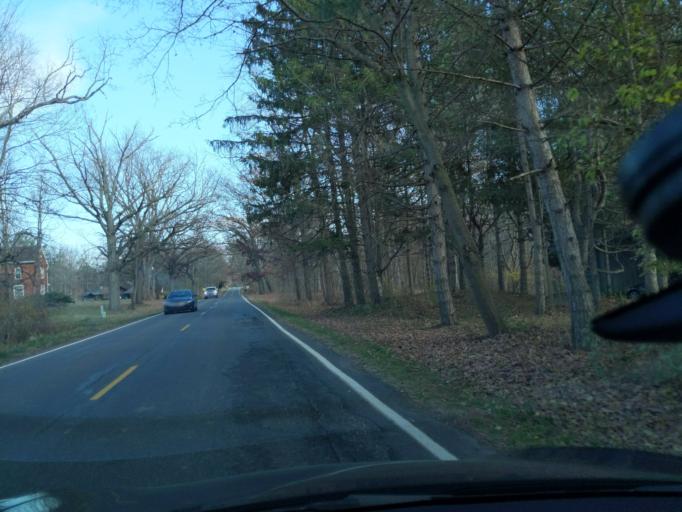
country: US
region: Michigan
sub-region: Ingham County
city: Haslett
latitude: 42.7154
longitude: -84.3467
